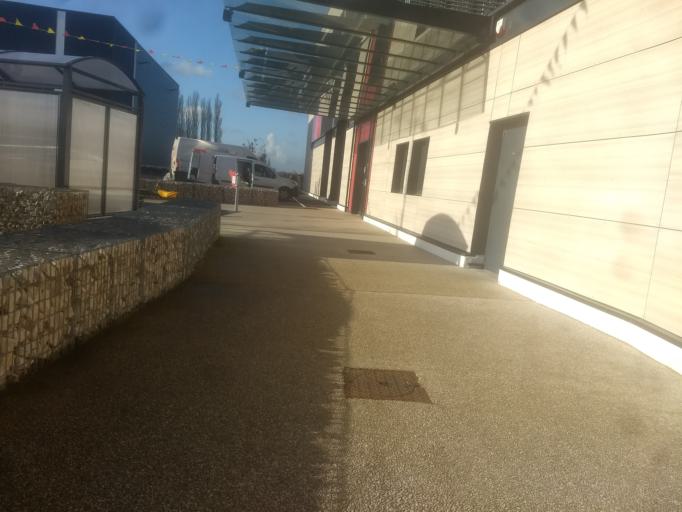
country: FR
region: Nord-Pas-de-Calais
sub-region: Departement du Pas-de-Calais
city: Anzin-Saint-Aubin
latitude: 50.3067
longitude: 2.7249
